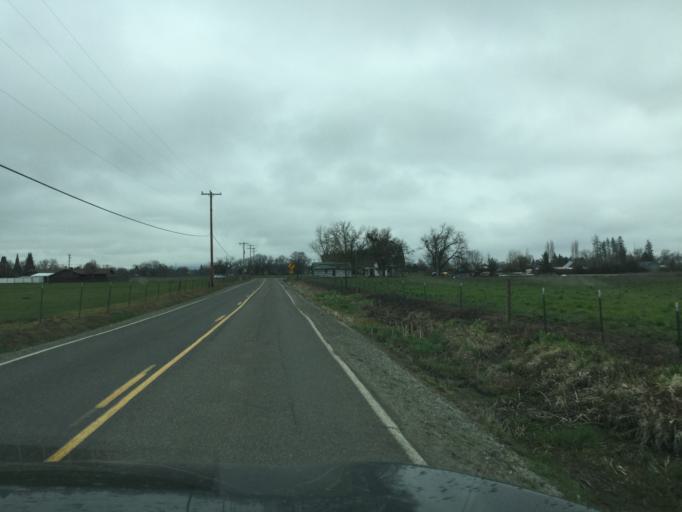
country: US
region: Oregon
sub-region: Jackson County
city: Central Point
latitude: 42.3898
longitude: -122.9441
